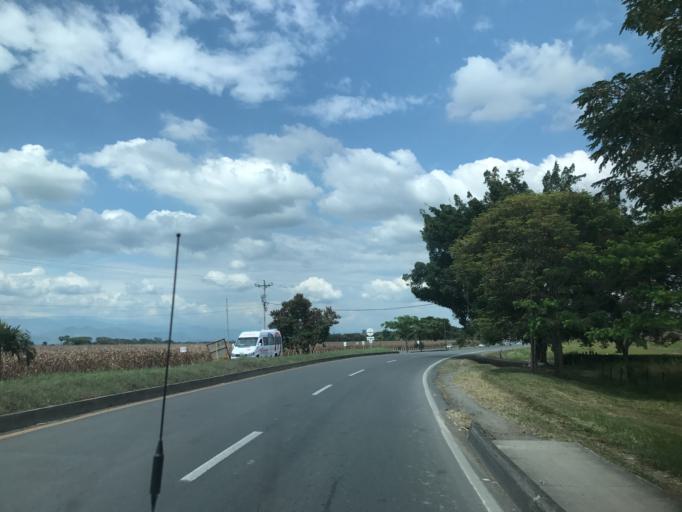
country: CO
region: Valle del Cauca
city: Obando
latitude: 4.5848
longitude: -75.9702
